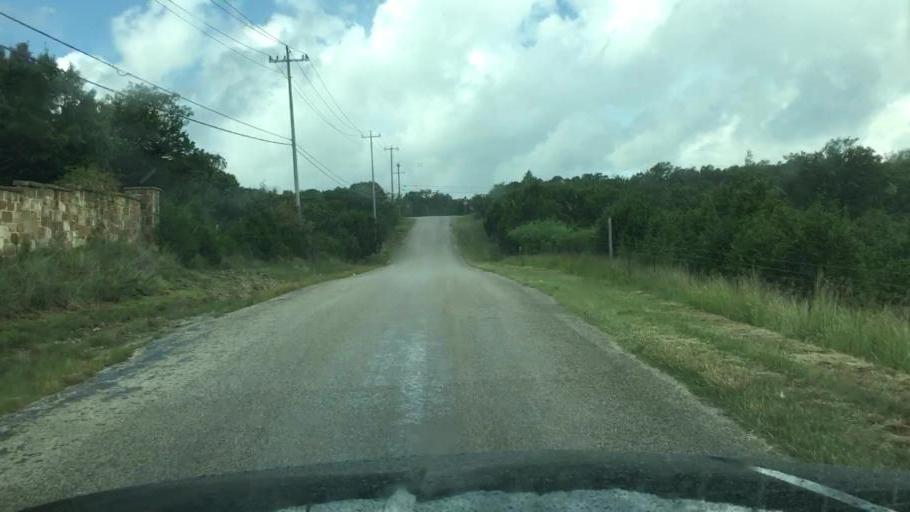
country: US
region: Texas
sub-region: Travis County
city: Bee Cave
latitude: 30.2035
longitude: -97.9700
